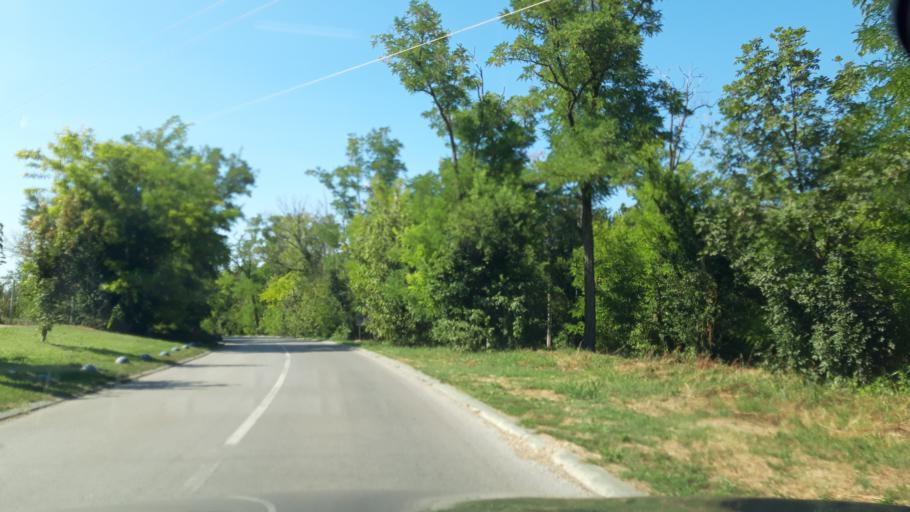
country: RS
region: Autonomna Pokrajina Vojvodina
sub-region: Sremski Okrug
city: Ruma
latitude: 45.0272
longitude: 19.8213
